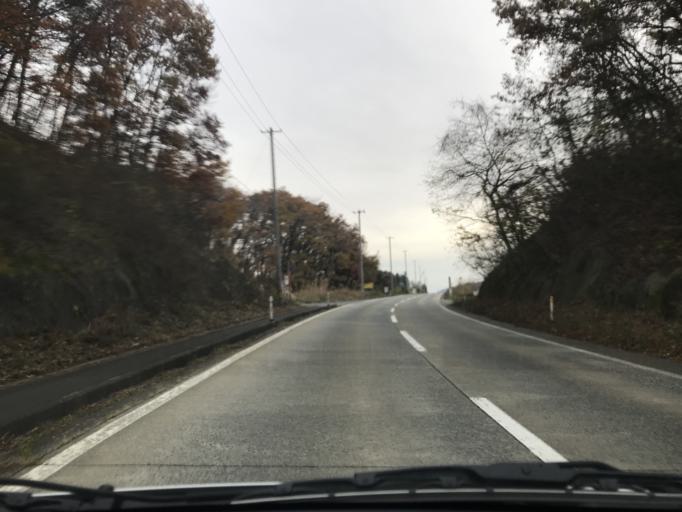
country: JP
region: Iwate
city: Kitakami
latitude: 39.2944
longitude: 141.2118
